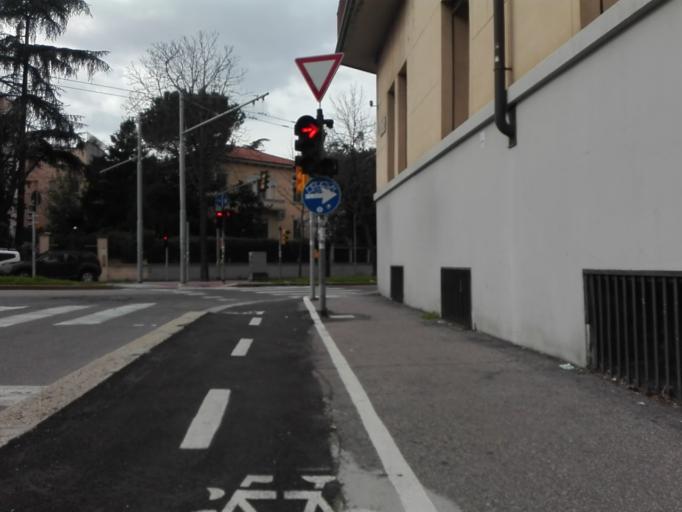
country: IT
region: Emilia-Romagna
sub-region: Provincia di Bologna
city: Bologna
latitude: 44.4862
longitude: 11.3583
